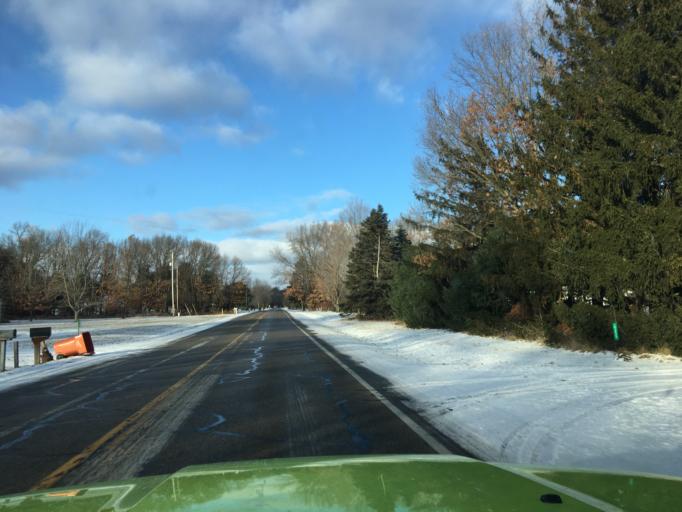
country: US
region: Michigan
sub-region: Montcalm County
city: Greenville
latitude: 43.2013
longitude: -85.2826
